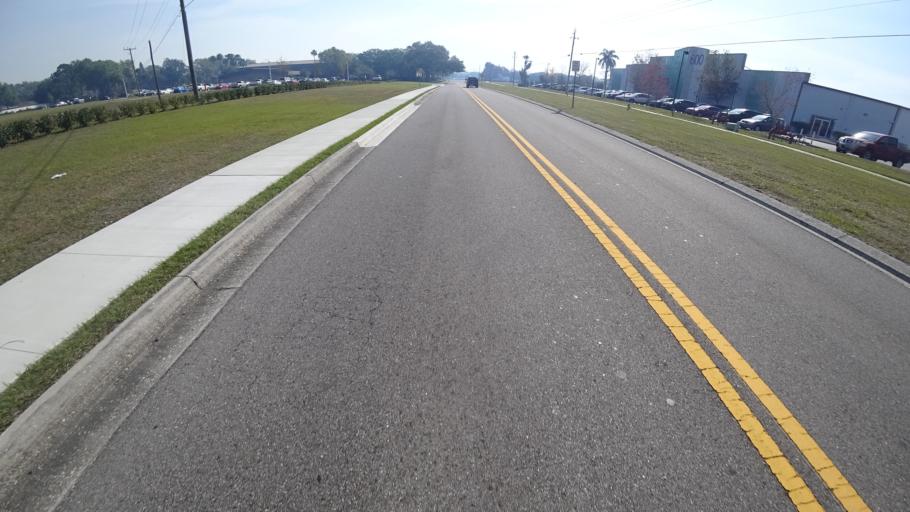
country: US
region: Florida
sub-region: Manatee County
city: Whitfield
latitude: 27.4077
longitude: -82.5624
